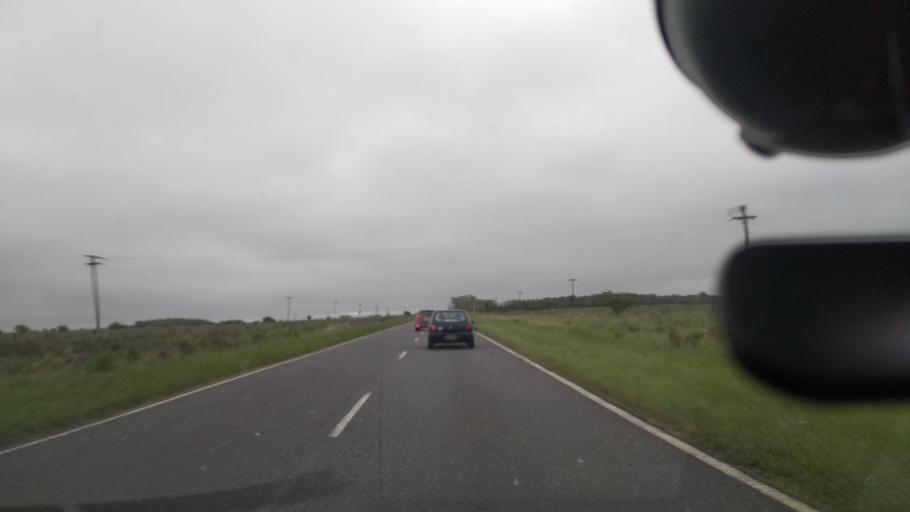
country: AR
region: Buenos Aires
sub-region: Partido de Magdalena
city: Magdalena
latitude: -35.2442
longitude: -57.6800
